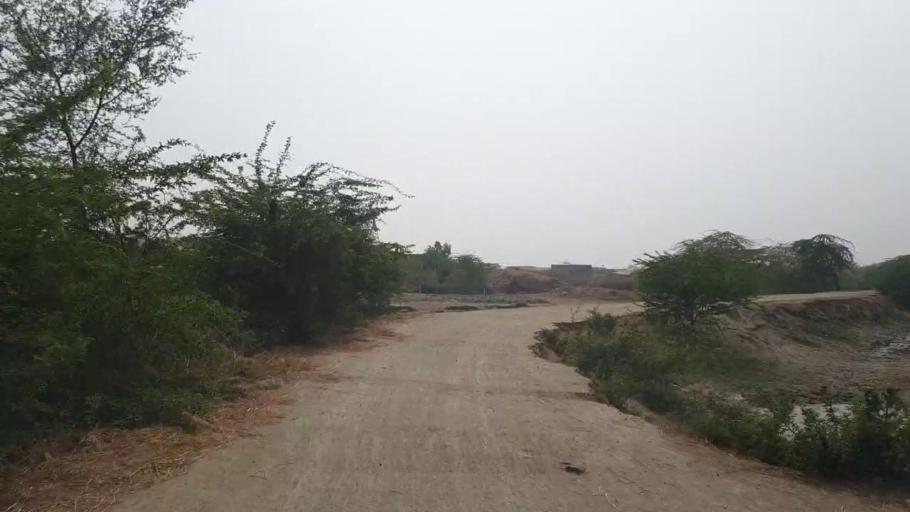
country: PK
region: Sindh
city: Kario
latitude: 24.6466
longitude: 68.6094
